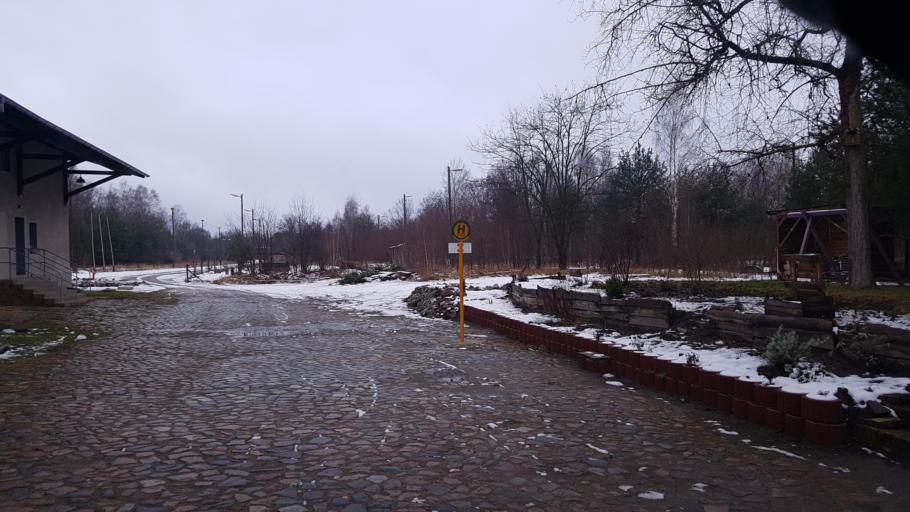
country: DE
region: Brandenburg
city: Jamlitz
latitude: 51.9930
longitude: 14.3706
